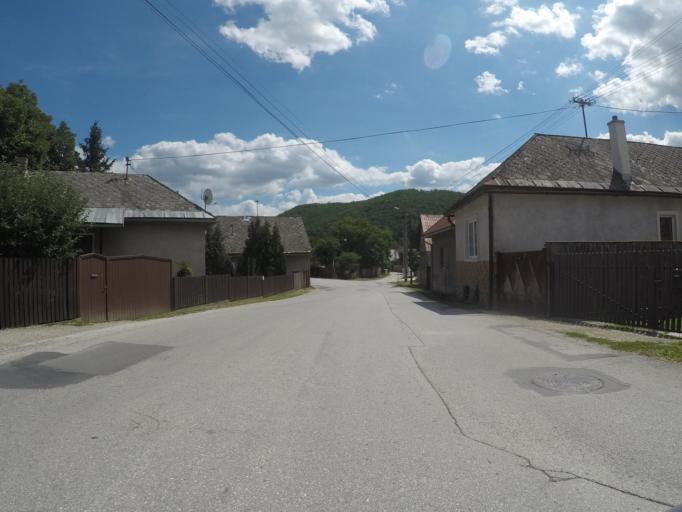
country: SK
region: Banskobystricky
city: Revuca
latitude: 48.7385
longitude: 20.0494
